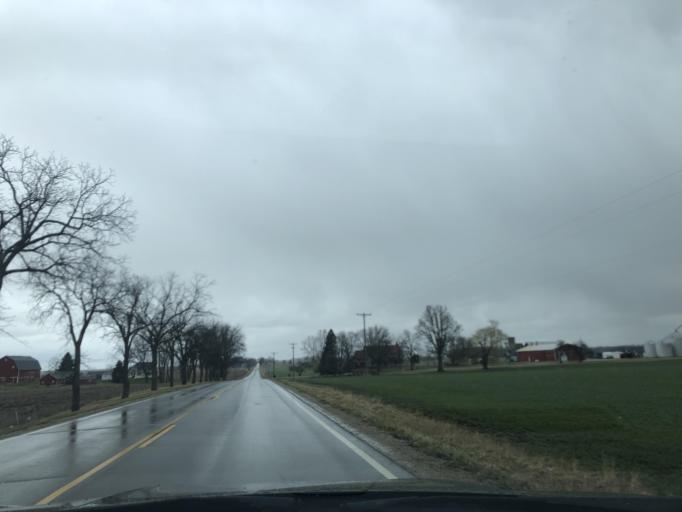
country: US
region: Michigan
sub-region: Clinton County
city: Fowler
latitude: 42.9489
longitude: -84.6608
